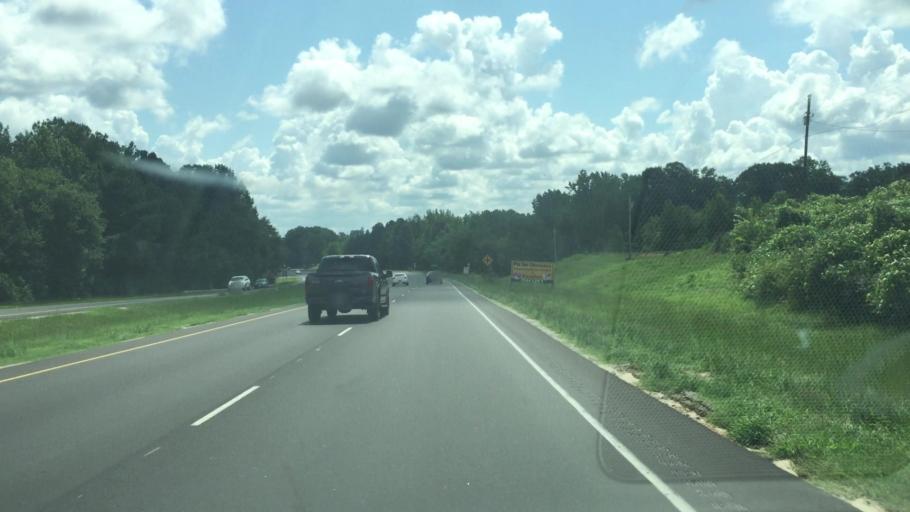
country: US
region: North Carolina
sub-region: Richmond County
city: Cordova
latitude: 34.9450
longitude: -79.8908
